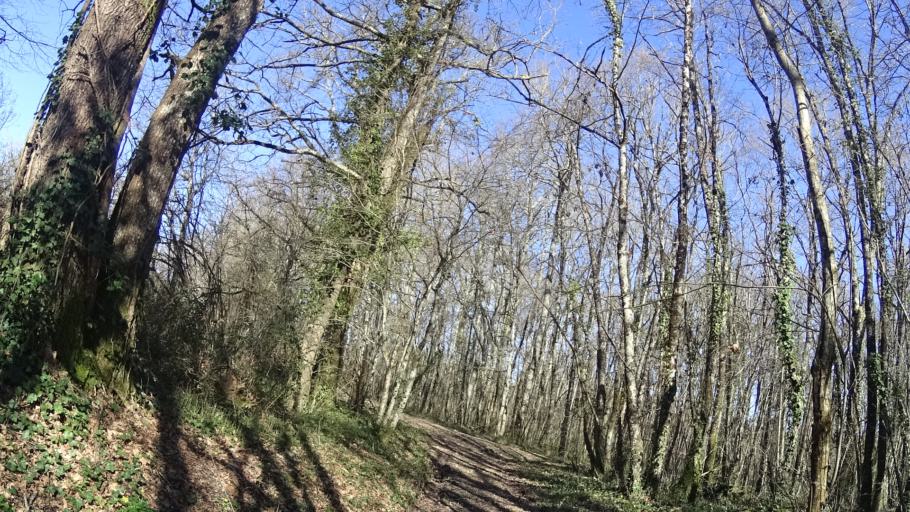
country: FR
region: Aquitaine
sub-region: Departement de la Dordogne
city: Saint-Aulaye
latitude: 45.2293
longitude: 0.1173
